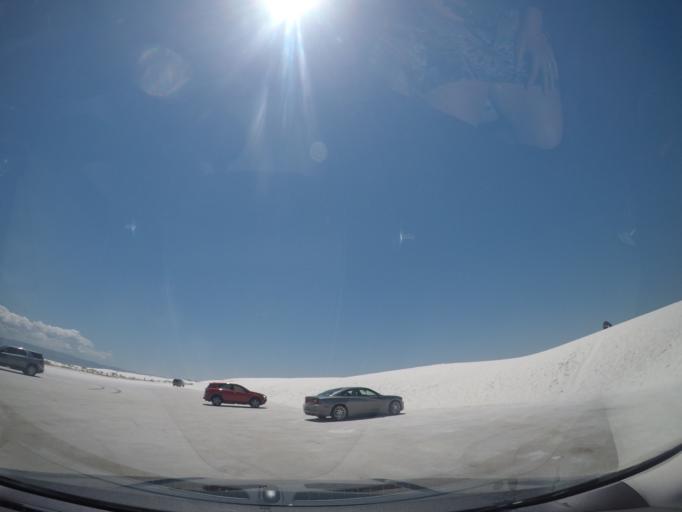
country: US
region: New Mexico
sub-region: Otero County
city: Holloman Air Force Base
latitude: 32.8064
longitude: -106.2614
